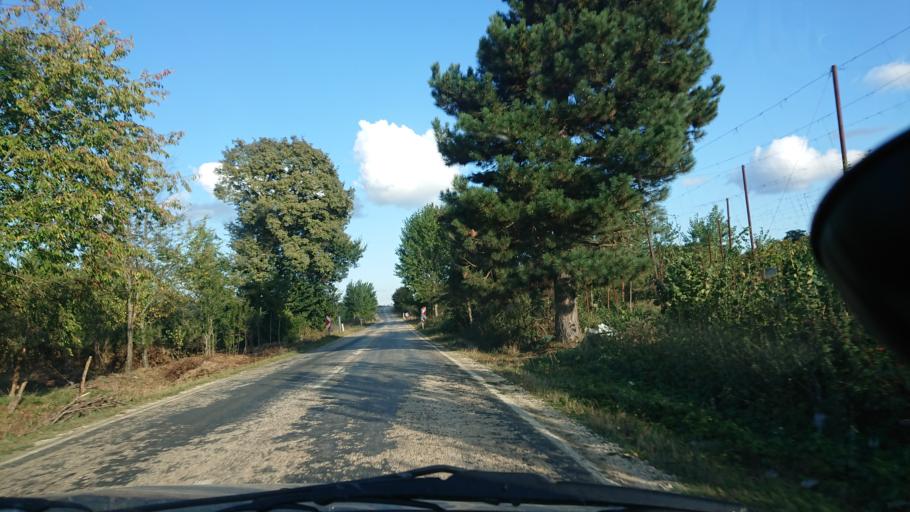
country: TR
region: Bilecik
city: Pazaryeri
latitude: 40.0144
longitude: 29.8465
